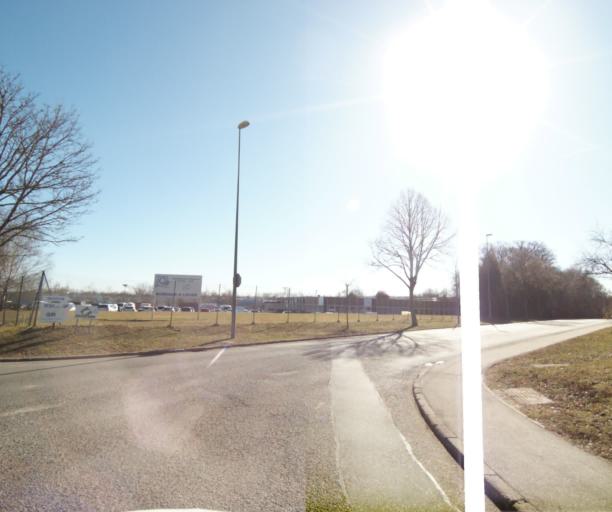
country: FR
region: Lorraine
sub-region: Departement de Meurthe-et-Moselle
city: Richardmenil
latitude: 48.6125
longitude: 6.1859
